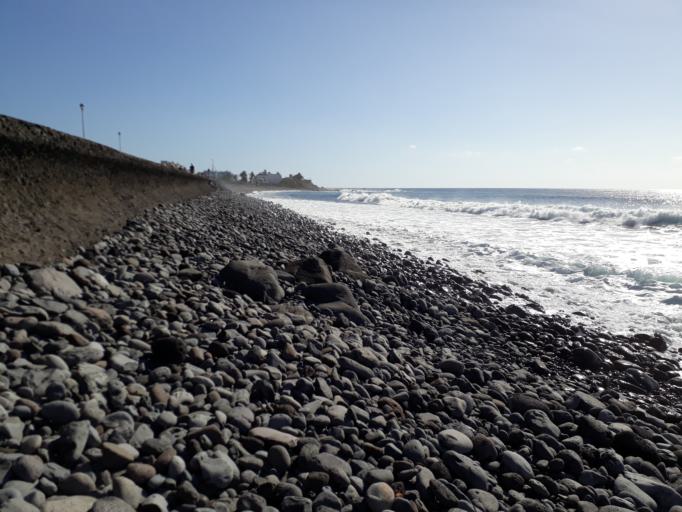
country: ES
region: Canary Islands
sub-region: Provincia de Santa Cruz de Tenerife
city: Alajero
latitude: 28.0926
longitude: -17.3406
